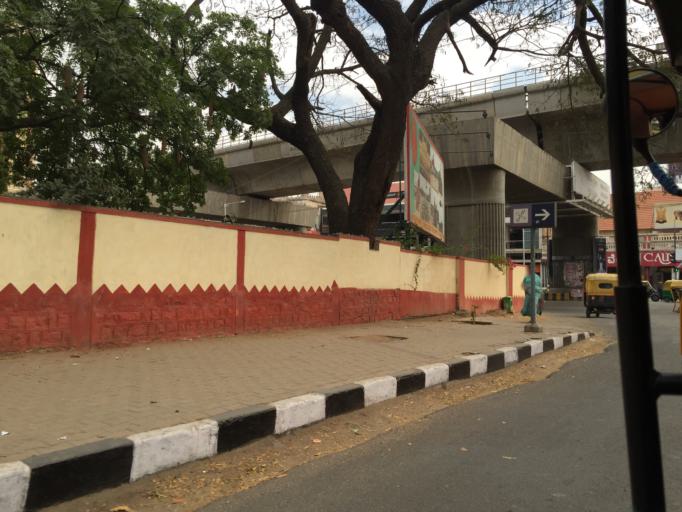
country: IN
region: Karnataka
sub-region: Bangalore Urban
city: Bangalore
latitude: 12.9757
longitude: 77.6082
